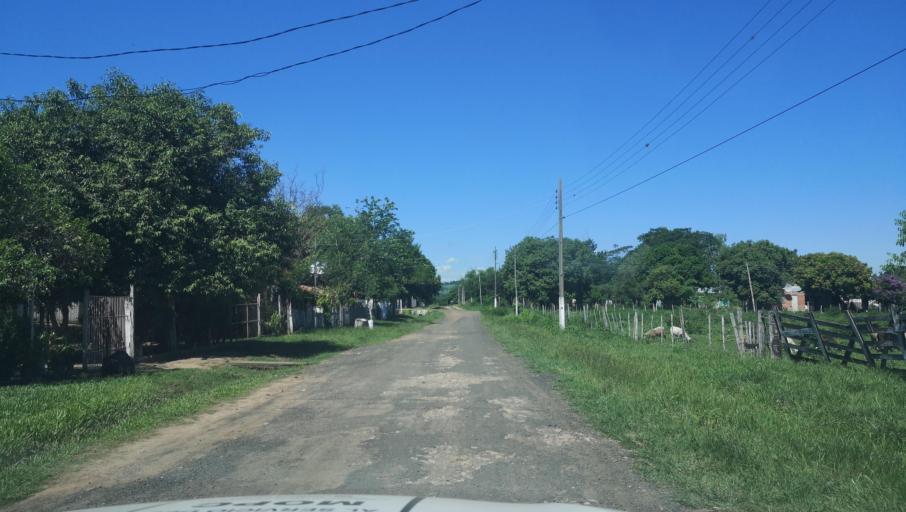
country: PY
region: Caaguazu
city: Carayao
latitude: -25.2063
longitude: -56.3982
